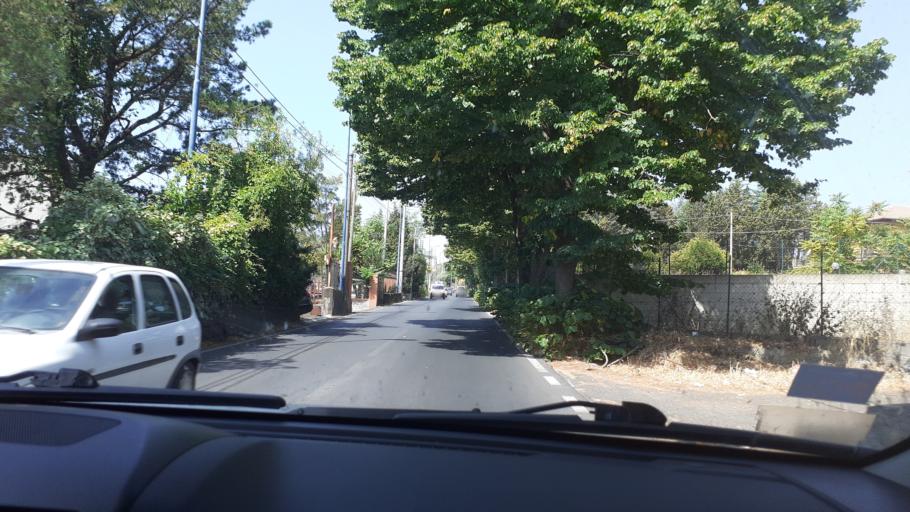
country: IT
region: Sicily
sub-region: Catania
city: Pedara
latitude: 37.6155
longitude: 15.0464
